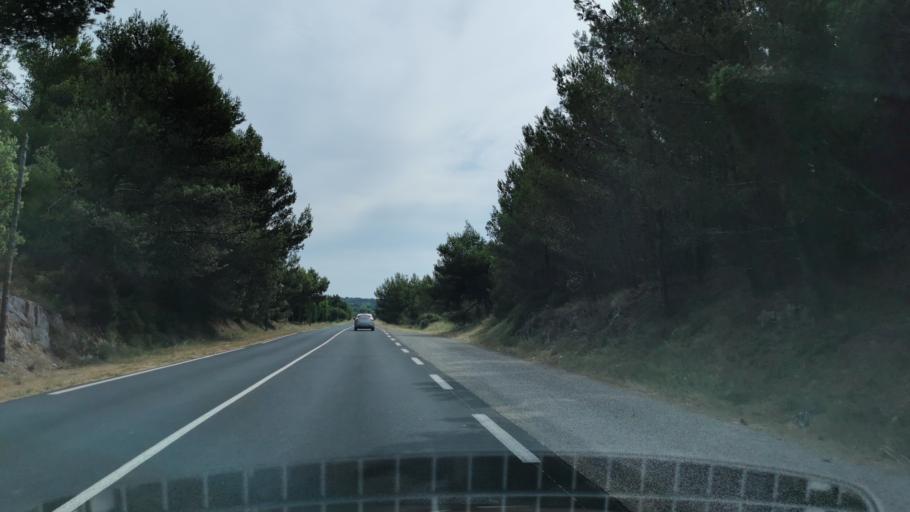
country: FR
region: Languedoc-Roussillon
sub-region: Departement de l'Aude
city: Canet
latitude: 43.2781
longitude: 2.8038
